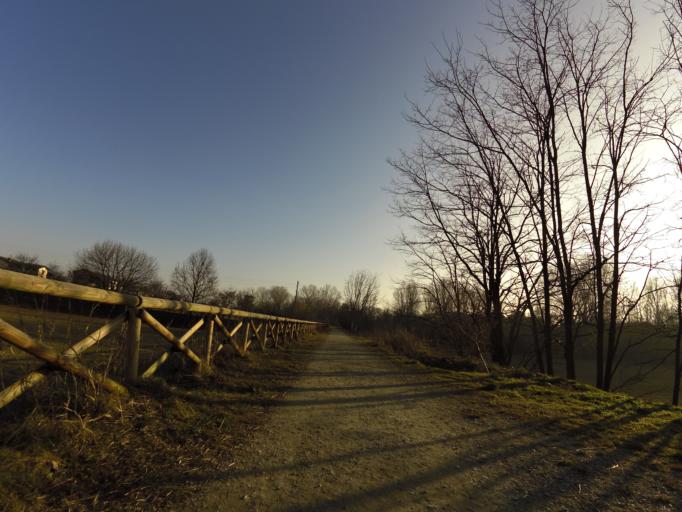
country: IT
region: Lombardy
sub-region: Citta metropolitana di Milano
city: Melegnano
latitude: 45.3673
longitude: 9.3287
